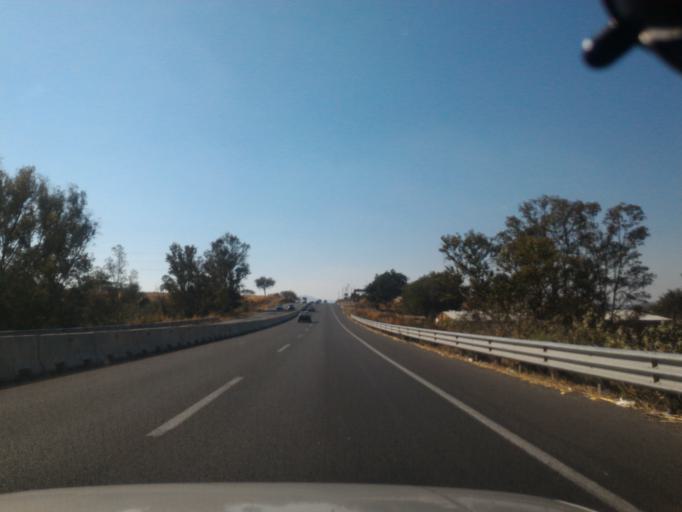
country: MX
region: Jalisco
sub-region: Poncitlan
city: Santa Cruz el Grande
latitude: 20.3654
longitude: -102.8237
